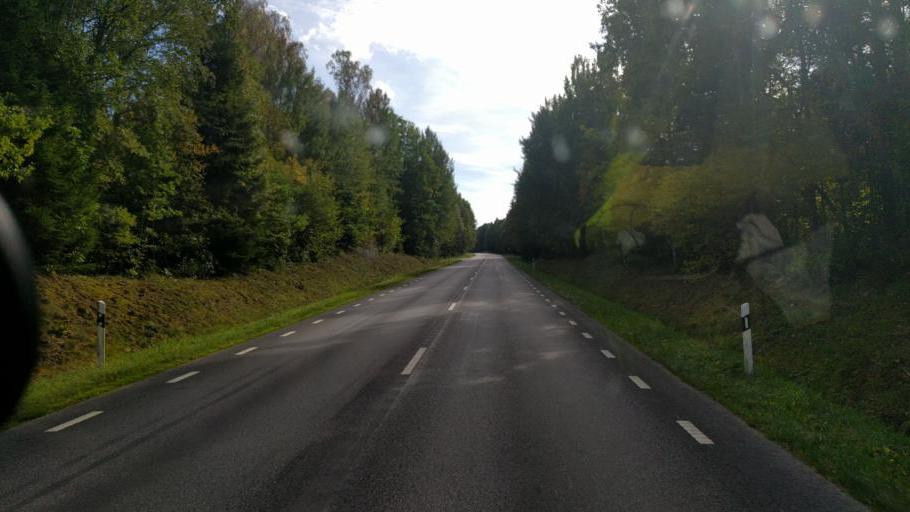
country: SE
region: OEstergoetland
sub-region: Kinda Kommun
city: Kisa
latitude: 57.9431
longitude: 15.6669
